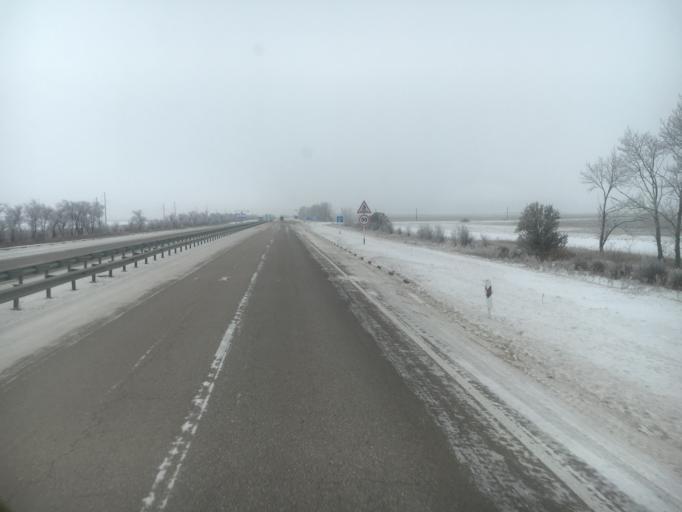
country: KZ
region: Aqmola
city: Akkol'
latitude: 53.3410
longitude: 69.5076
